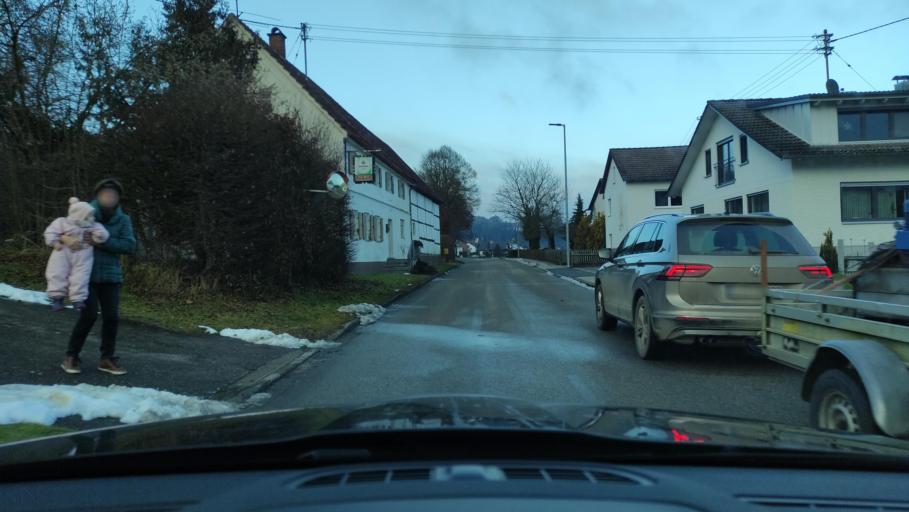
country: DE
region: Bavaria
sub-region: Swabia
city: Deisenhausen
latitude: 48.2958
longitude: 10.3562
